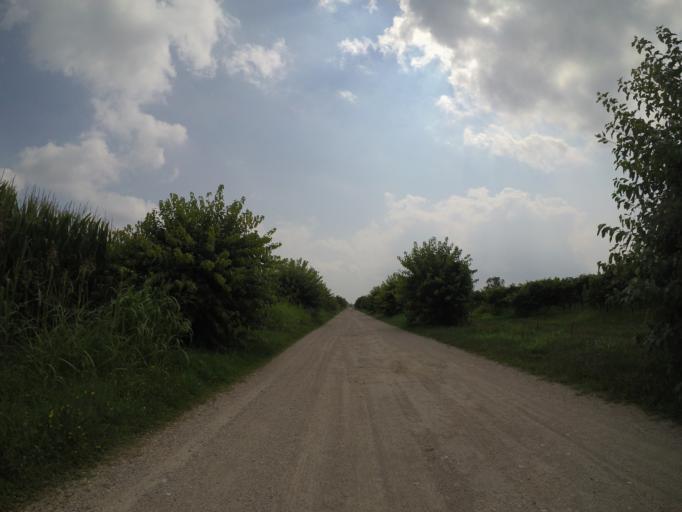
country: IT
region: Friuli Venezia Giulia
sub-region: Provincia di Udine
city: Codroipo
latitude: 45.9883
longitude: 13.0109
